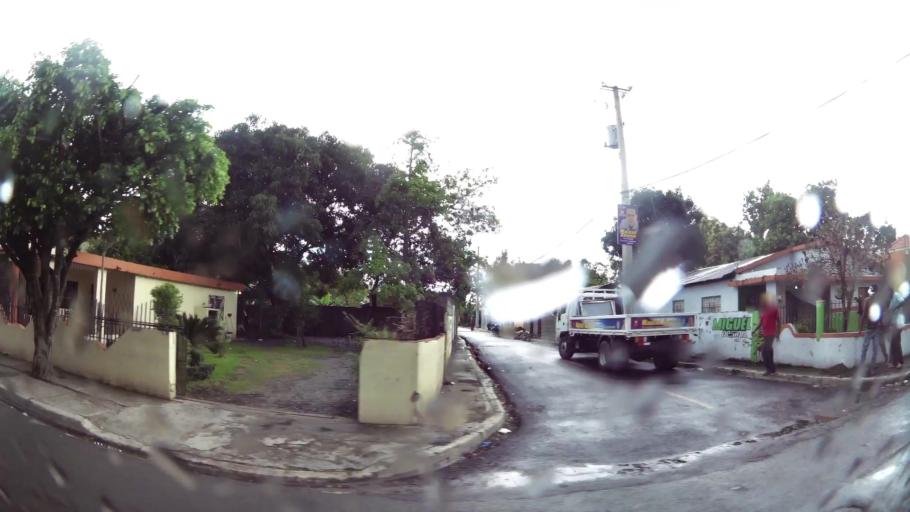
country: DO
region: Monsenor Nouel
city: Bonao
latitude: 18.9341
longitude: -70.4037
